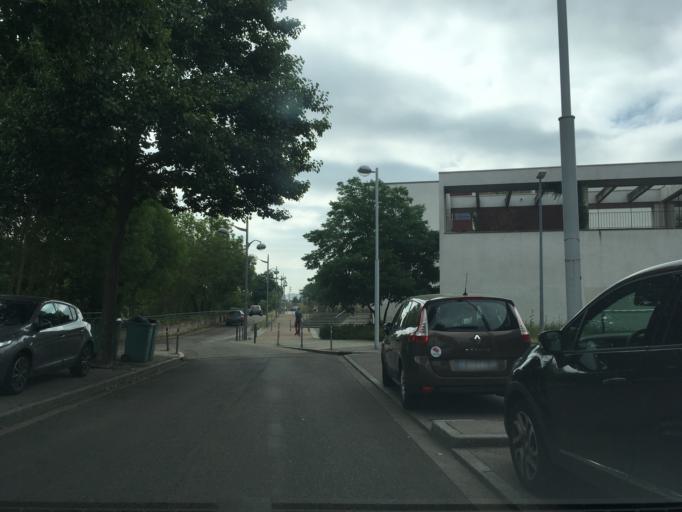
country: FR
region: Lorraine
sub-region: Departement de Meurthe-et-Moselle
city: Saint-Max
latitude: 48.6955
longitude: 6.1974
